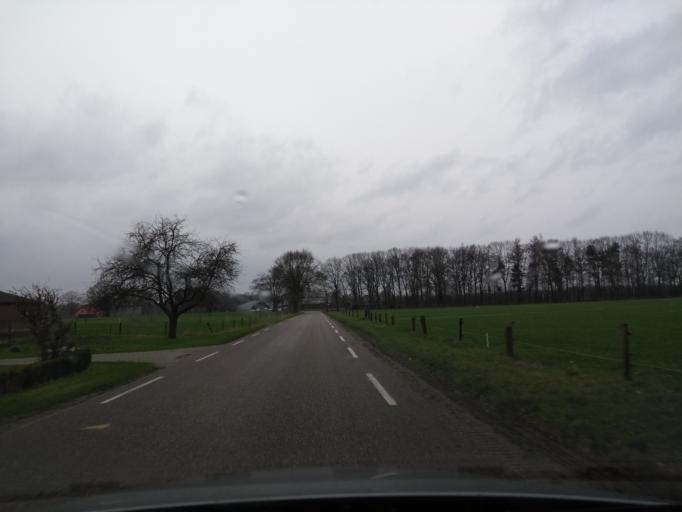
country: NL
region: Gelderland
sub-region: Gemeente Bronckhorst
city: Zelhem
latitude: 52.0538
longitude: 6.4040
